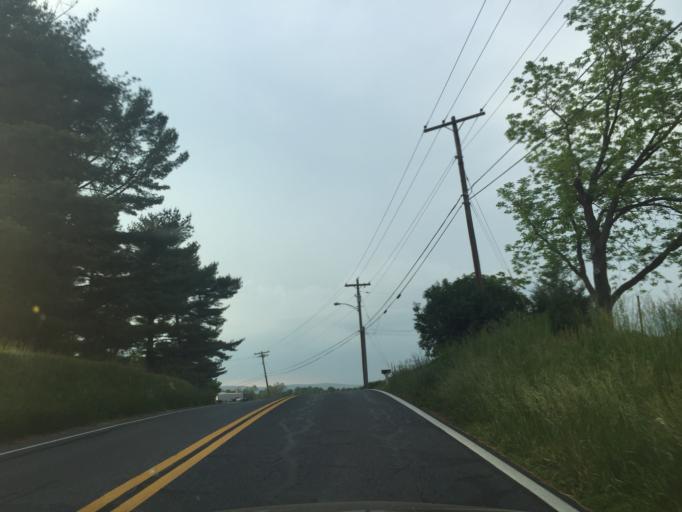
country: US
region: Maryland
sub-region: Frederick County
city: Brunswick
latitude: 39.3218
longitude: -77.6155
